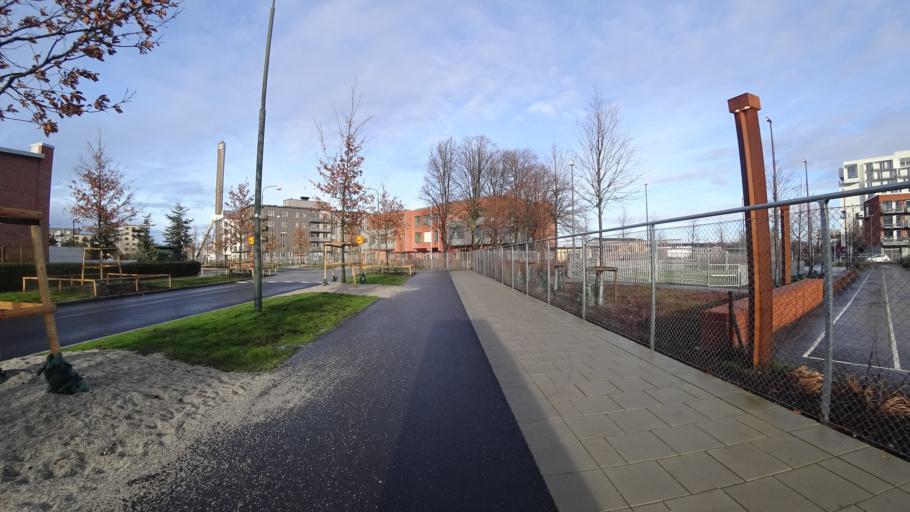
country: SE
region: Skane
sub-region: Malmo
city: Bunkeflostrand
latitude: 55.5875
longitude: 12.9347
